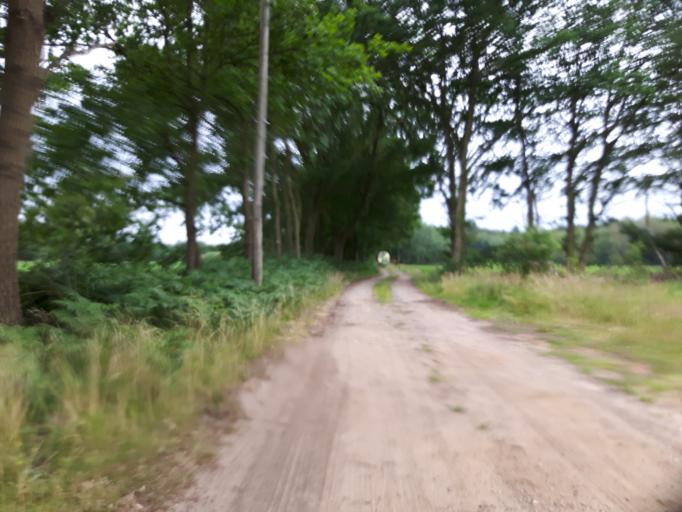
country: DE
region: Lower Saxony
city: Vierhofen
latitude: 53.2693
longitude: 10.1894
